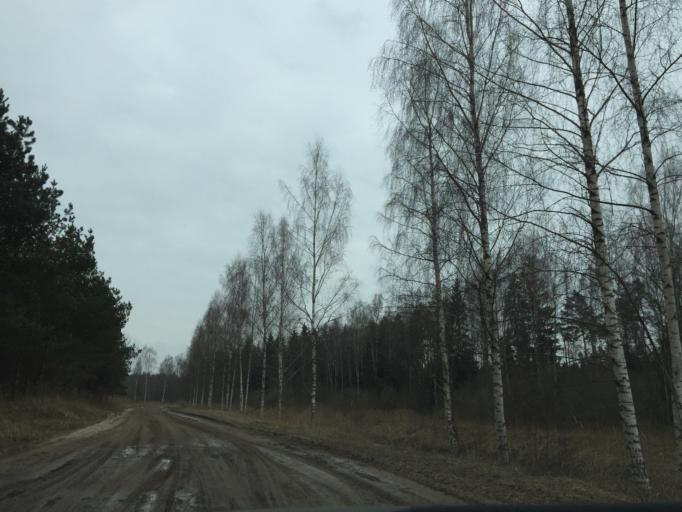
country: LV
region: Kekava
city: Balozi
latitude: 56.7818
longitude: 24.1229
